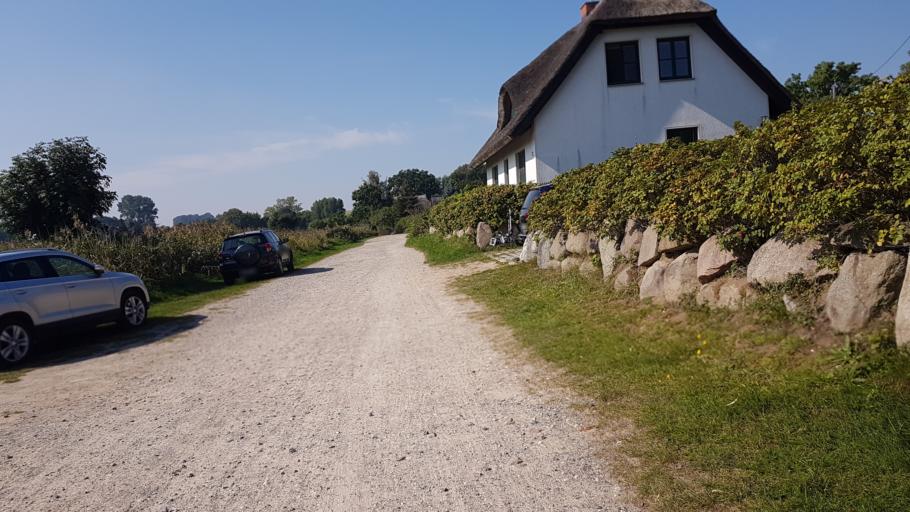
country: DE
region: Mecklenburg-Vorpommern
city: Ostseebad Binz
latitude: 54.3531
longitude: 13.5780
